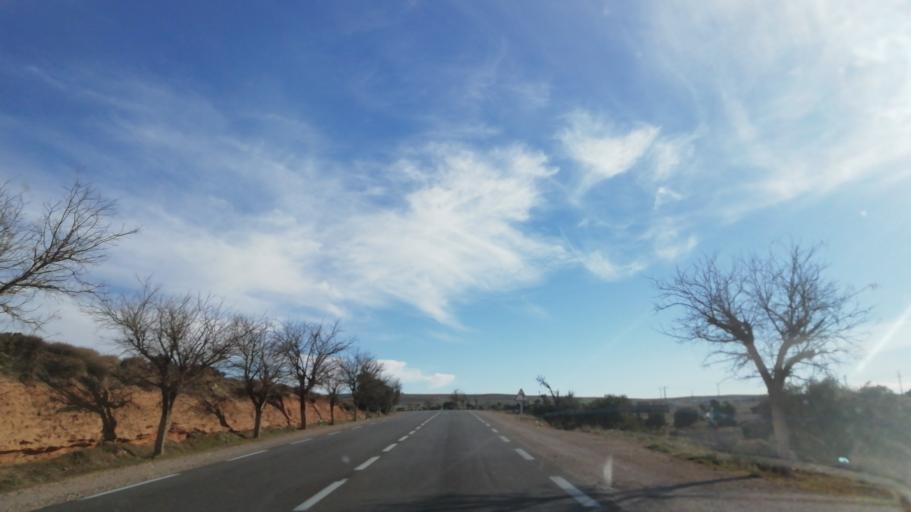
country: DZ
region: Tlemcen
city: Sebdou
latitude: 34.5684
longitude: -1.3189
